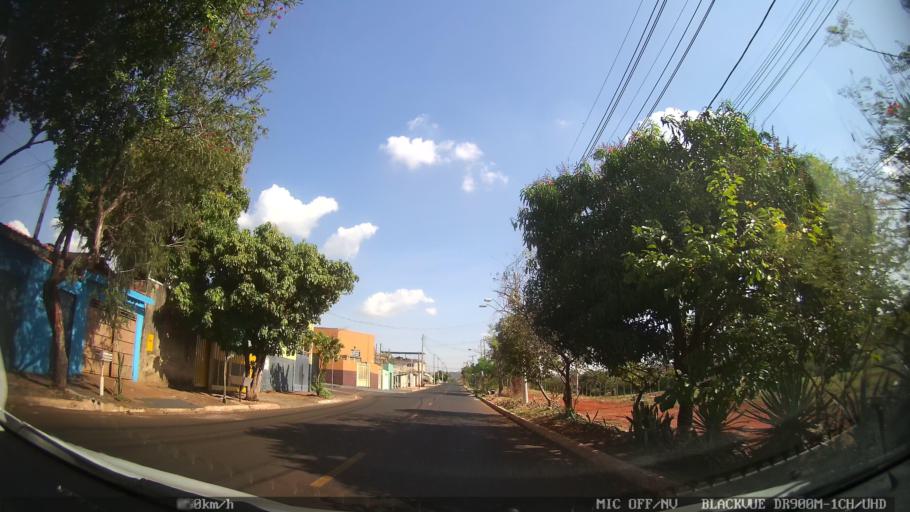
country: BR
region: Sao Paulo
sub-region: Ribeirao Preto
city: Ribeirao Preto
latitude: -21.1990
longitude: -47.8548
